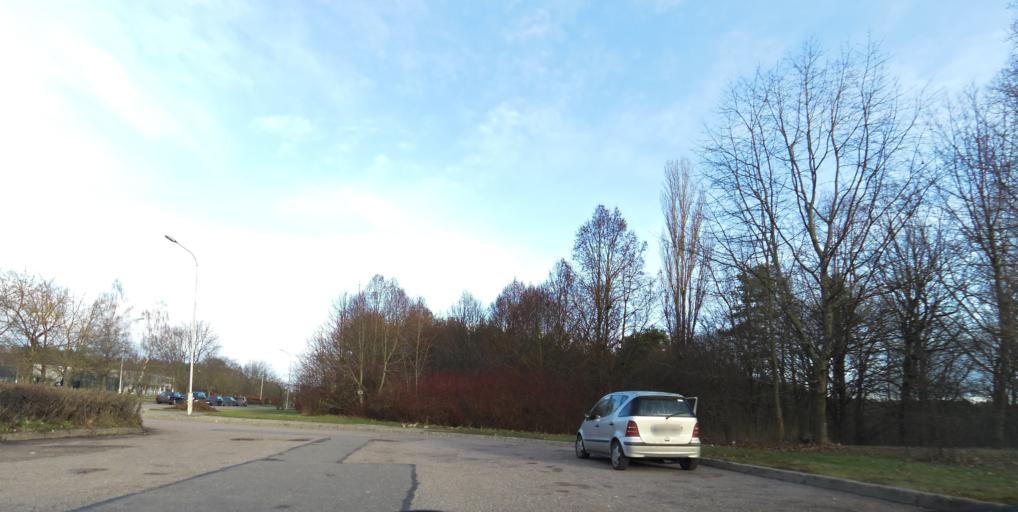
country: LT
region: Vilnius County
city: Justiniskes
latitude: 54.6966
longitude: 25.2293
